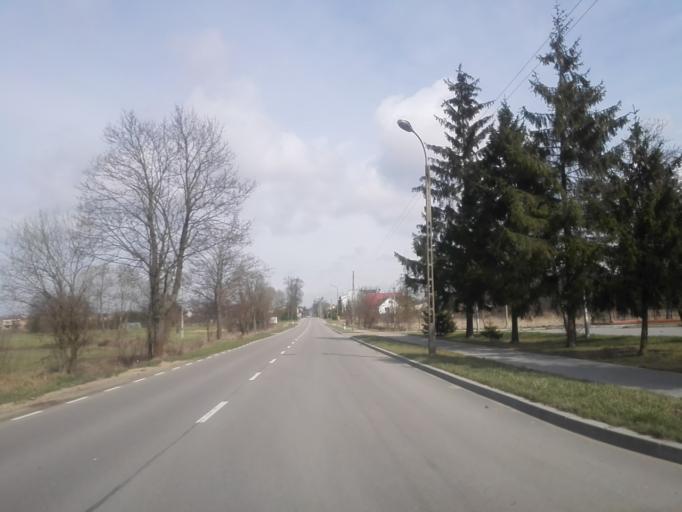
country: PL
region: Podlasie
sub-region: Powiat sejnenski
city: Sejny
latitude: 54.0975
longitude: 23.3480
